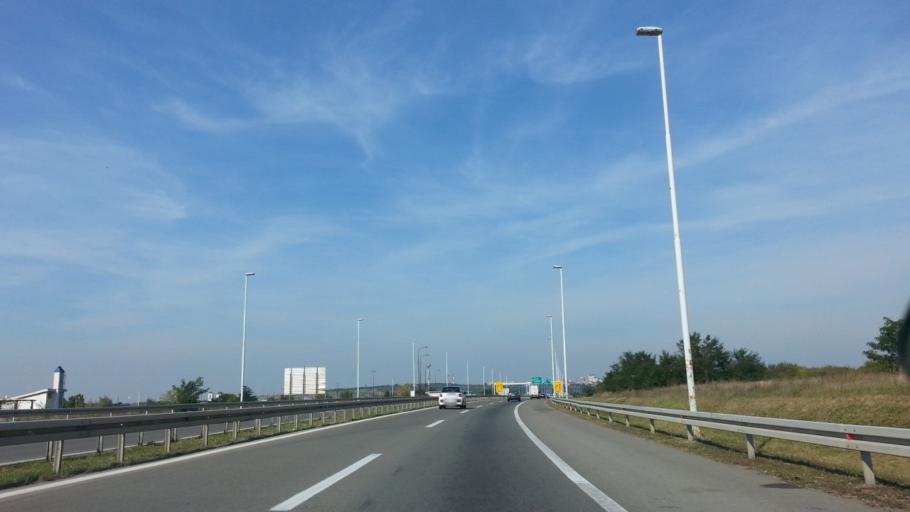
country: RS
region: Central Serbia
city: Sremcica
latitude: 44.7041
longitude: 20.4132
